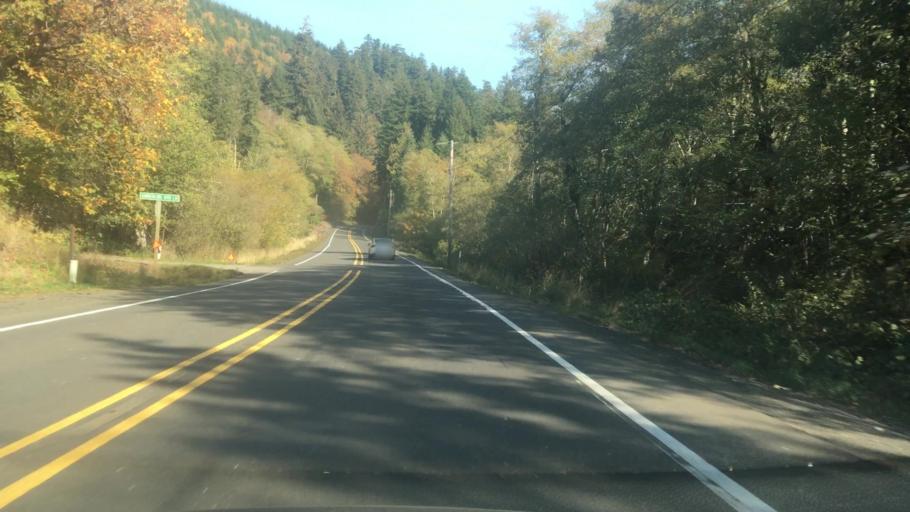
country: US
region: Oregon
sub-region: Lincoln County
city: Rose Lodge
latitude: 45.0239
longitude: -123.8280
